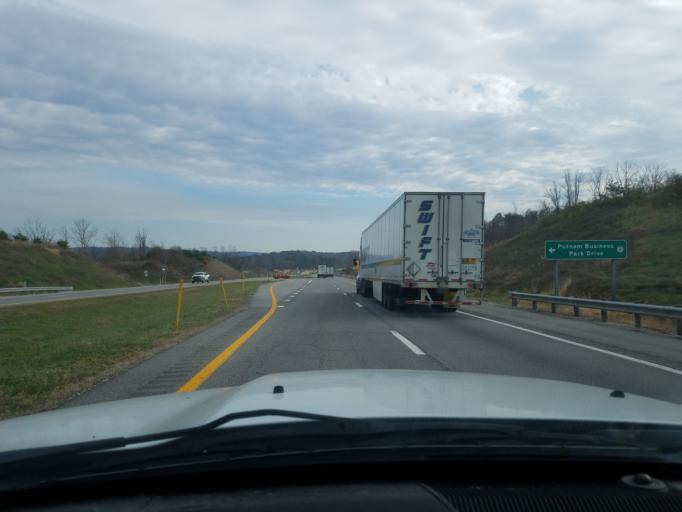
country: US
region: West Virginia
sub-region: Putnam County
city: Eleanor
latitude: 38.5505
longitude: -81.9856
